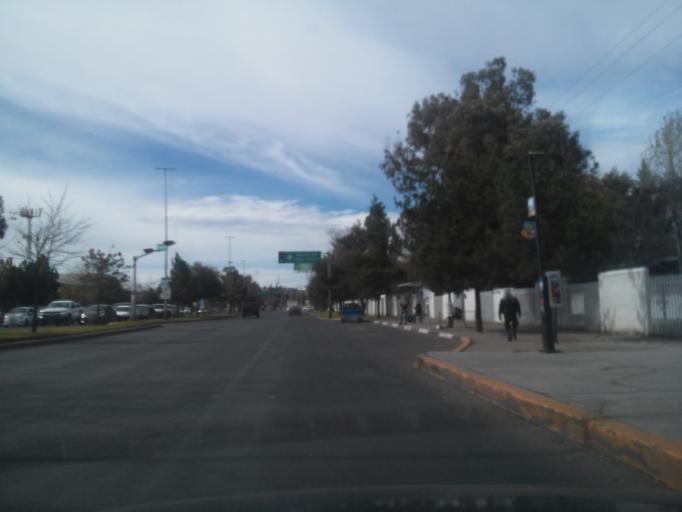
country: MX
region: Durango
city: Victoria de Durango
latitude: 24.0076
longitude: -104.6589
